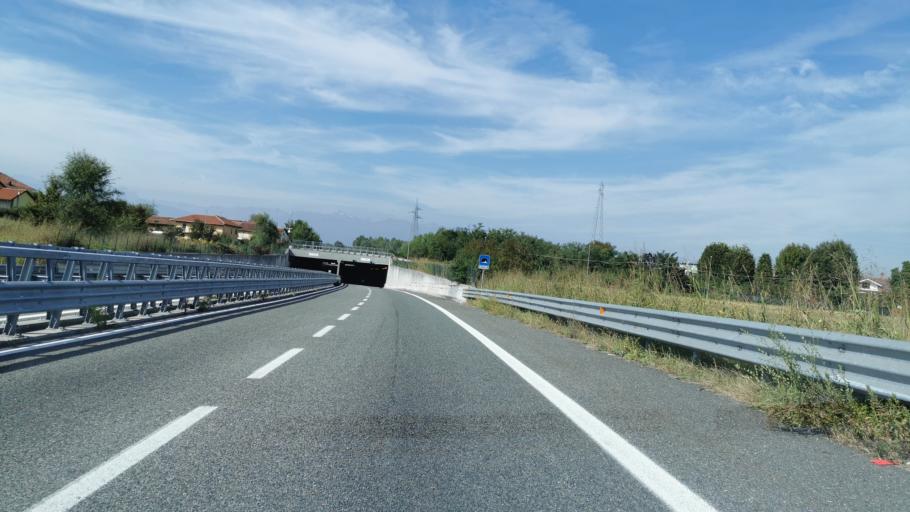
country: IT
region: Piedmont
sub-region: Provincia di Torino
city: Borgaro Torinese
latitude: 45.1415
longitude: 7.6537
